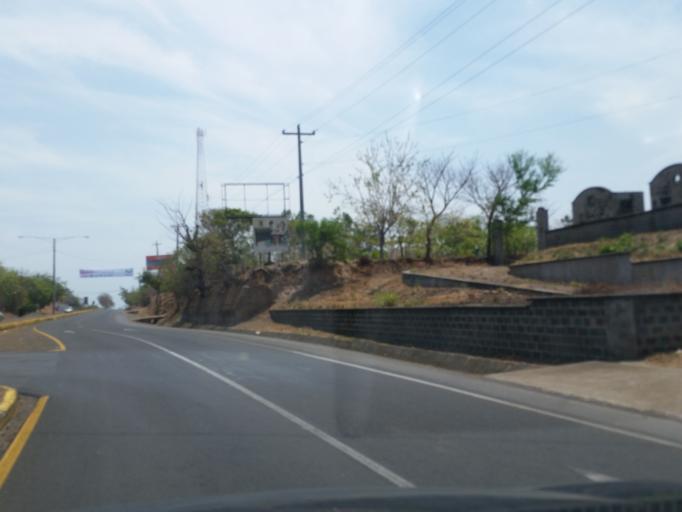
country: NI
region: Granada
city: Granada
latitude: 11.9590
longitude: -85.9923
